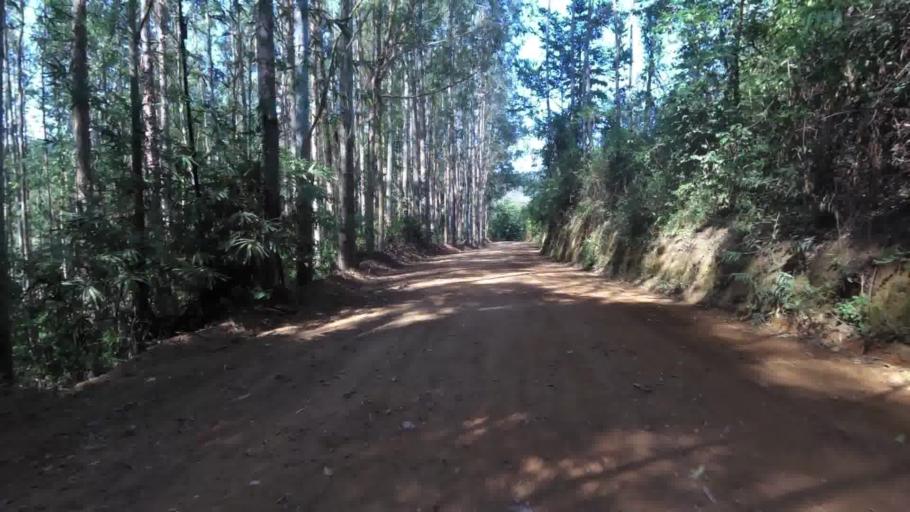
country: BR
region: Espirito Santo
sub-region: Alfredo Chaves
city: Alfredo Chaves
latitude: -20.5366
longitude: -40.8488
